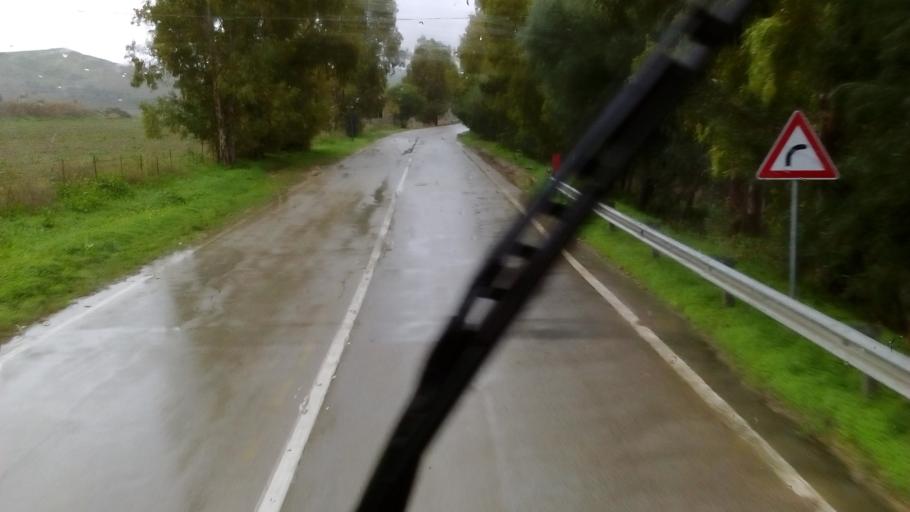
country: IT
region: Sicily
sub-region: Enna
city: Pietraperzia
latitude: 37.4924
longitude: 14.1510
